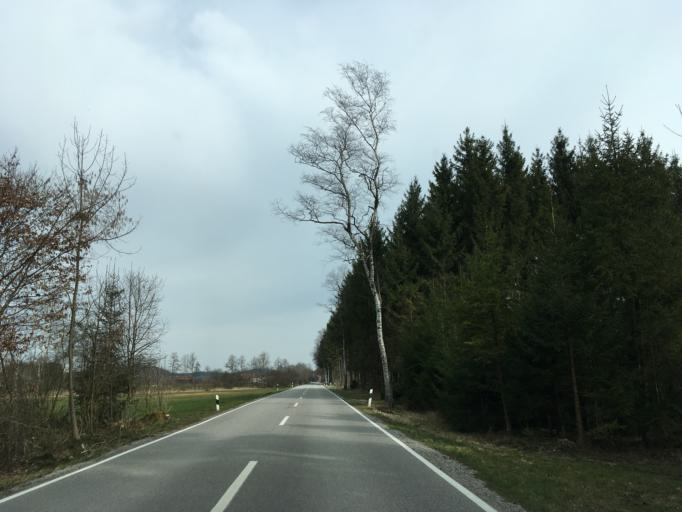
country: DE
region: Bavaria
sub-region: Upper Bavaria
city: Eggstatt
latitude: 47.9336
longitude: 12.3929
